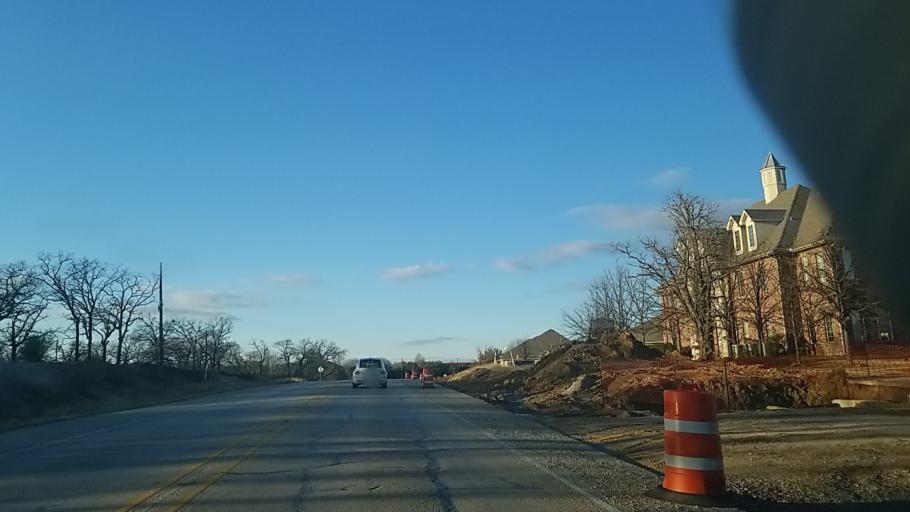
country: US
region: Texas
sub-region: Denton County
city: Denton
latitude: 33.1702
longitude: -97.1119
